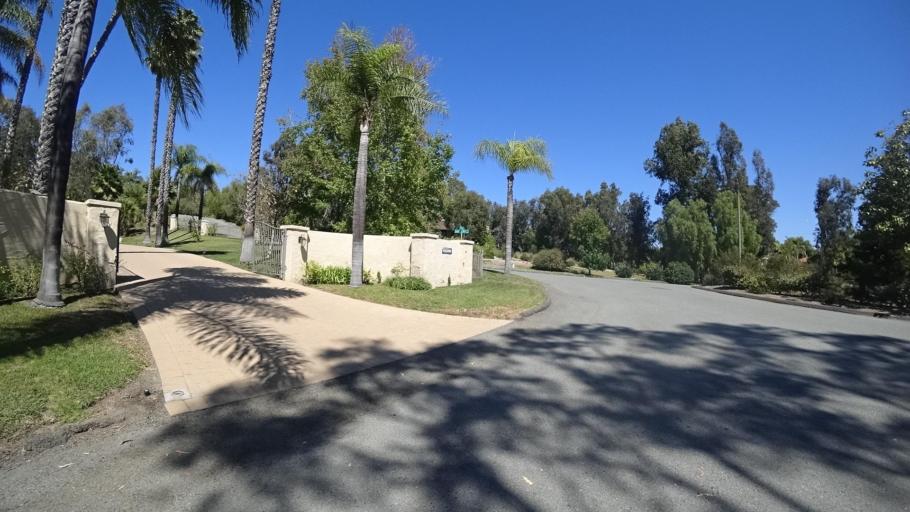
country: US
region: California
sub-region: San Diego County
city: Rancho Santa Fe
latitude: 33.0333
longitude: -117.1726
